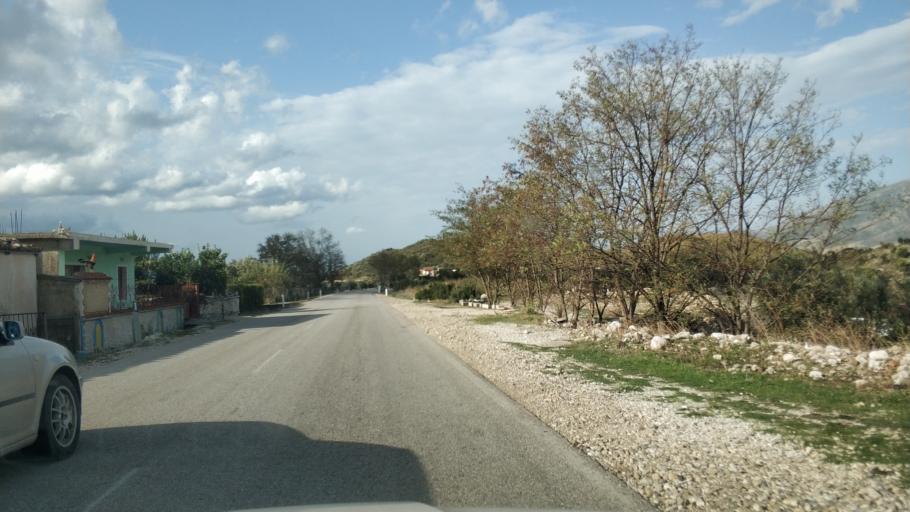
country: AL
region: Vlore
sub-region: Rrethi i Vlores
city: Orikum
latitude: 40.2921
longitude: 19.4916
